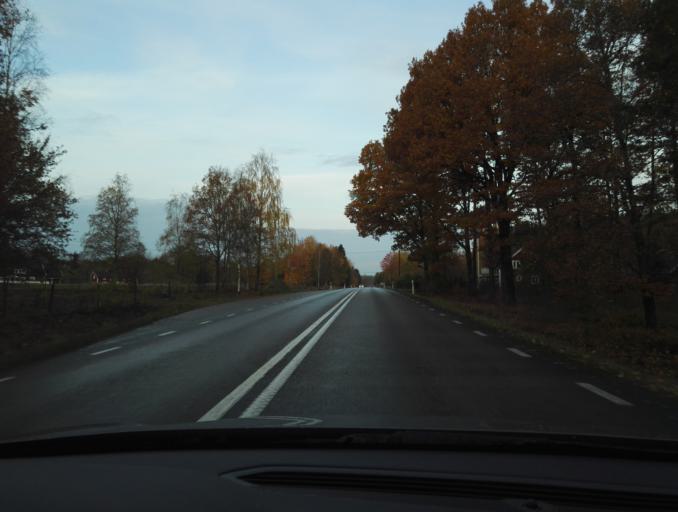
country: SE
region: Kronoberg
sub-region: Alvesta Kommun
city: Moheda
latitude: 56.9896
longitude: 14.6888
